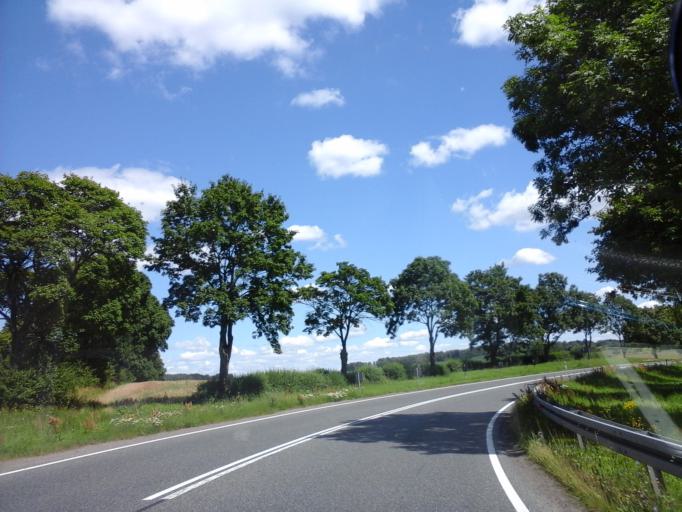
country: PL
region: West Pomeranian Voivodeship
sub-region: Powiat choszczenski
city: Recz
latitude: 53.2853
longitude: 15.6025
